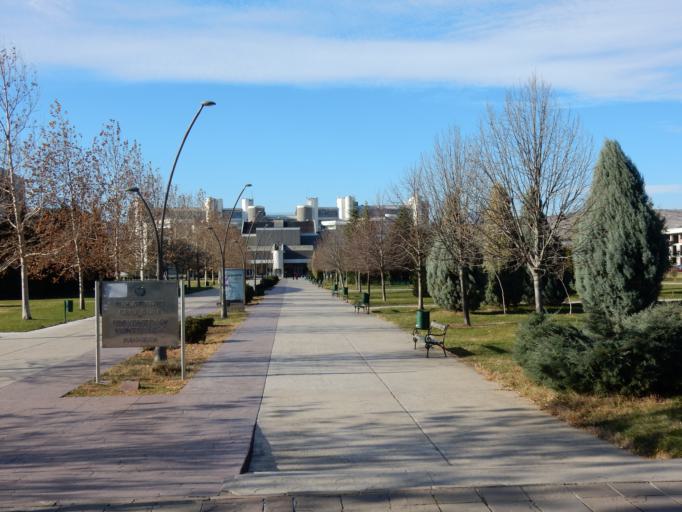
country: ME
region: Podgorica
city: Podgorica
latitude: 42.4422
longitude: 19.2438
